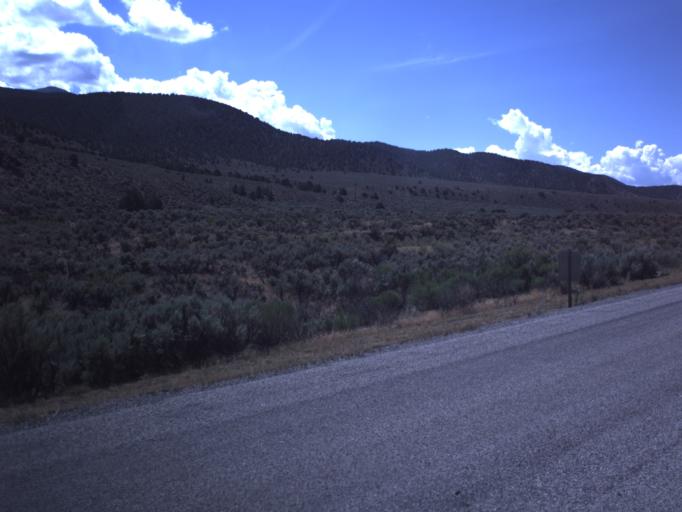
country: US
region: Utah
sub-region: Piute County
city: Junction
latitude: 38.0644
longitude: -112.3479
